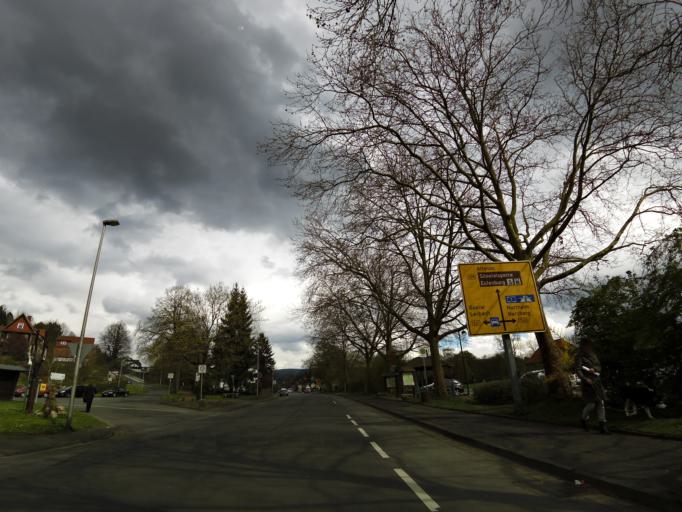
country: DE
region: Lower Saxony
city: Osterode am Harz
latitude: 51.7284
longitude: 10.2597
